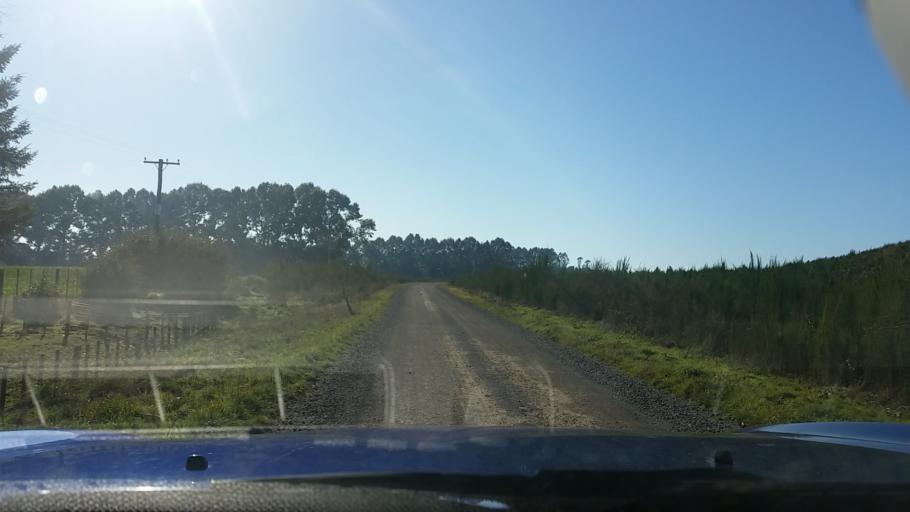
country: NZ
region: Bay of Plenty
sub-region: Whakatane District
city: Murupara
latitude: -38.3399
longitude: 176.5520
